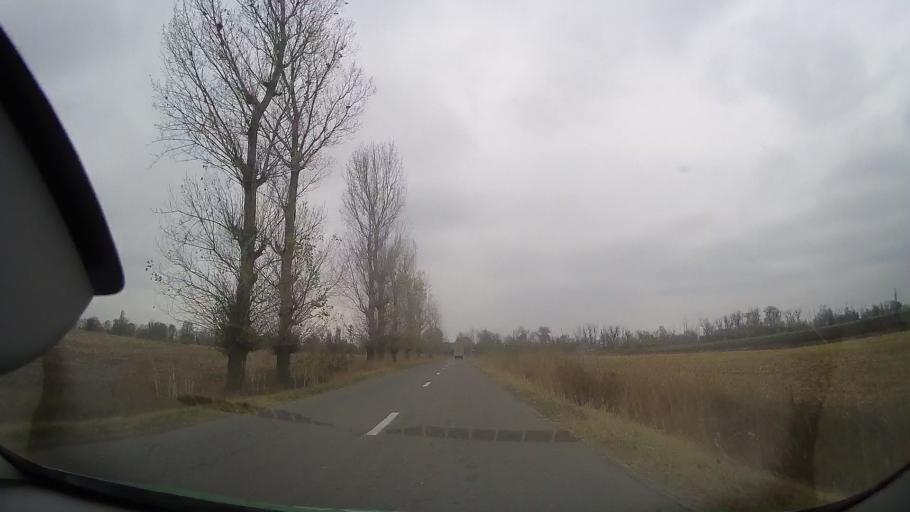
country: RO
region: Ialomita
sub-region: Comuna Garbovi
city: Garbovi
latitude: 44.7711
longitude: 26.7872
